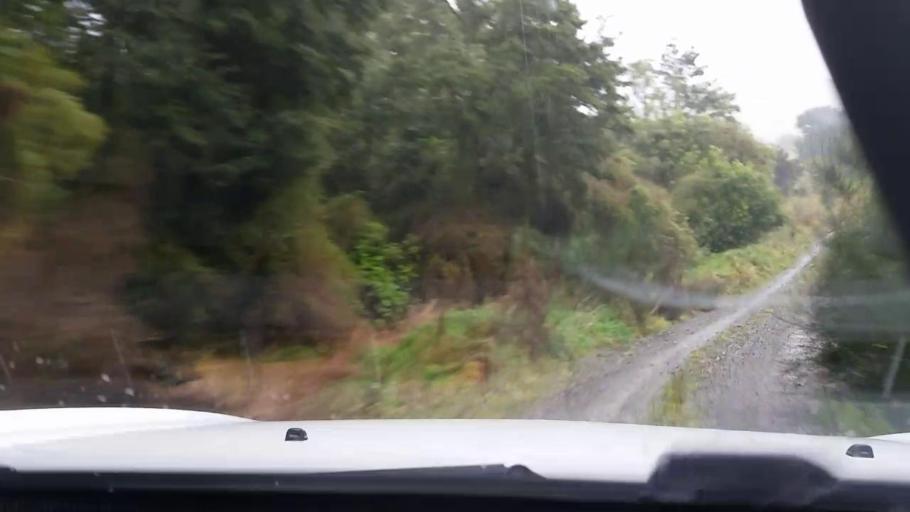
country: NZ
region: Wellington
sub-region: Masterton District
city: Masterton
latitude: -41.1605
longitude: 175.7963
